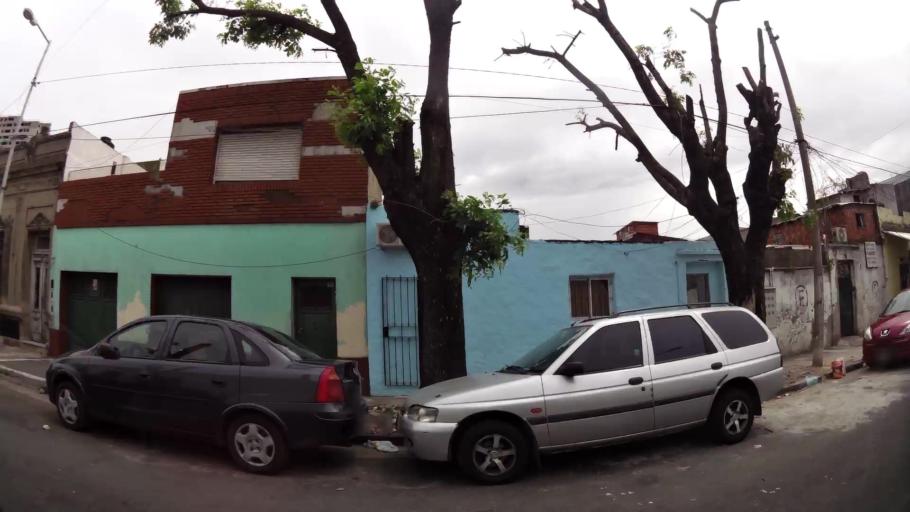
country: AR
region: Buenos Aires
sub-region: Partido de Avellaneda
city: Avellaneda
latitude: -34.6642
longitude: -58.3742
